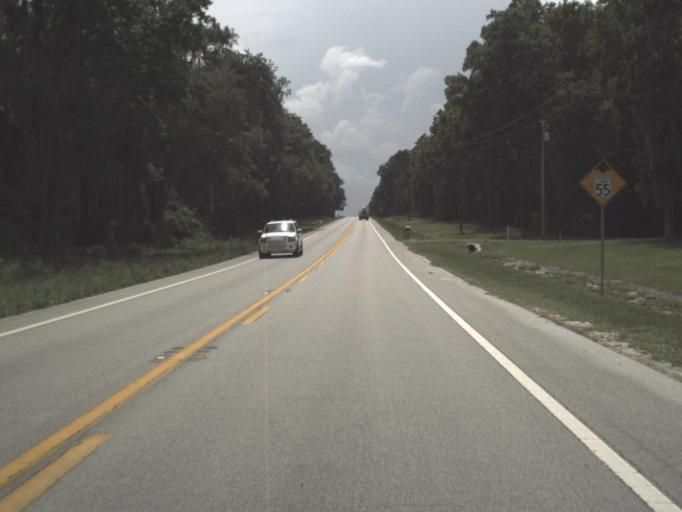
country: US
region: Florida
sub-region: Madison County
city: Madison
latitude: 30.4713
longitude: -83.3650
